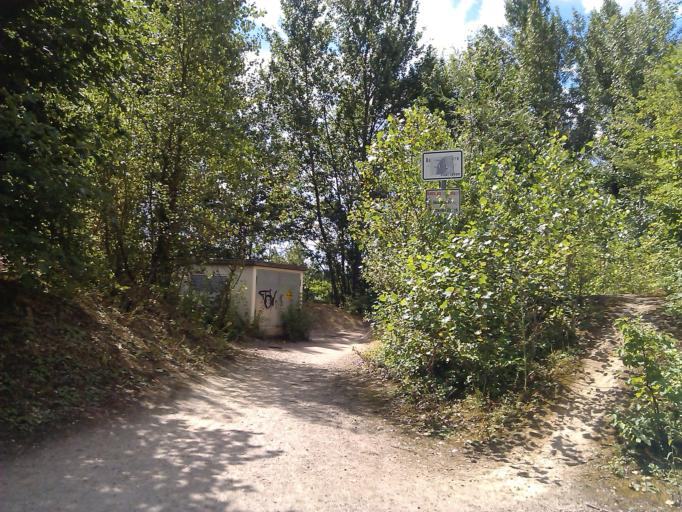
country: DE
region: Rheinland-Pfalz
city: Otterstadt
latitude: 49.3600
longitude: 8.4587
